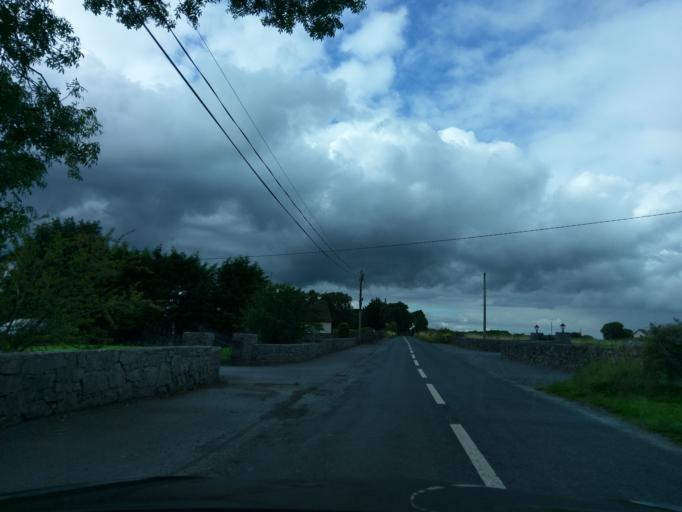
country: IE
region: Connaught
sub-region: County Galway
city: Athenry
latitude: 53.2724
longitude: -8.7434
